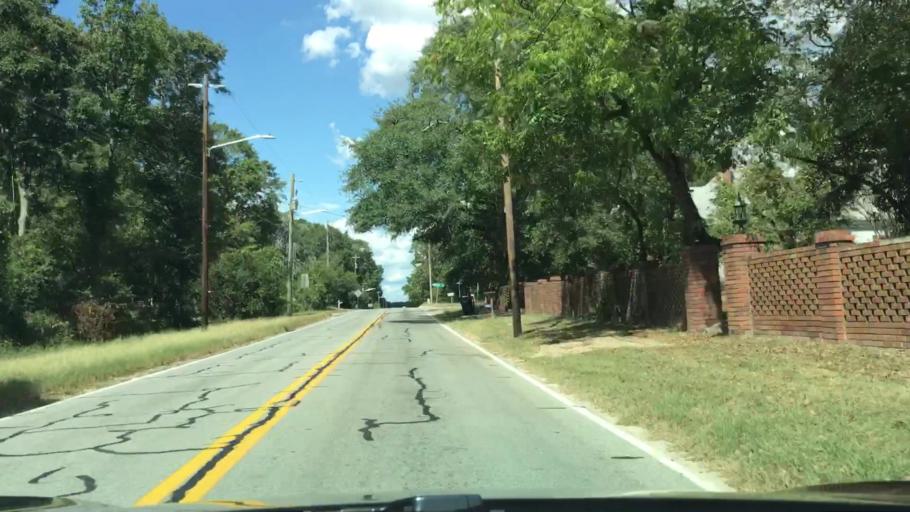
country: US
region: Georgia
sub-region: Greene County
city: Union Point
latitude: 33.5375
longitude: -83.0809
